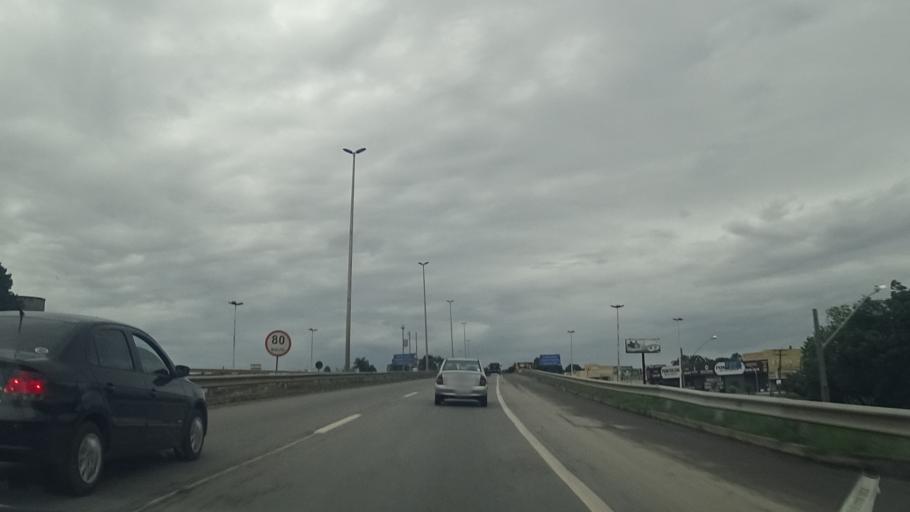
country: BR
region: Goias
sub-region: Goiania
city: Goiania
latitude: -16.7276
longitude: -49.2416
